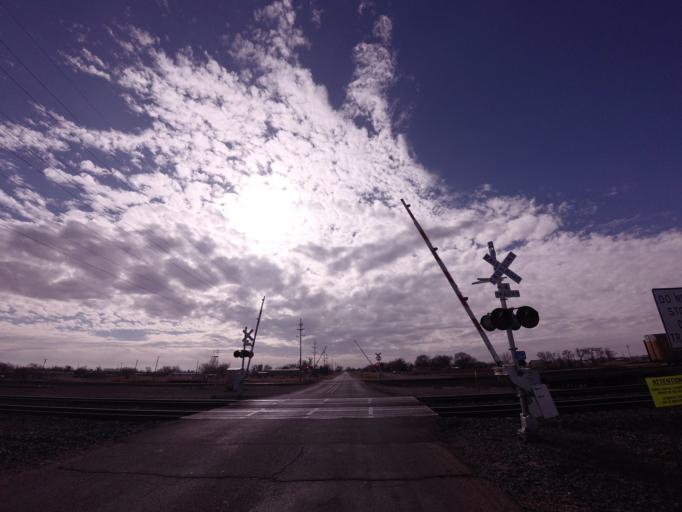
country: US
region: New Mexico
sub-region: Curry County
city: Clovis
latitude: 34.3992
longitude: -103.2318
